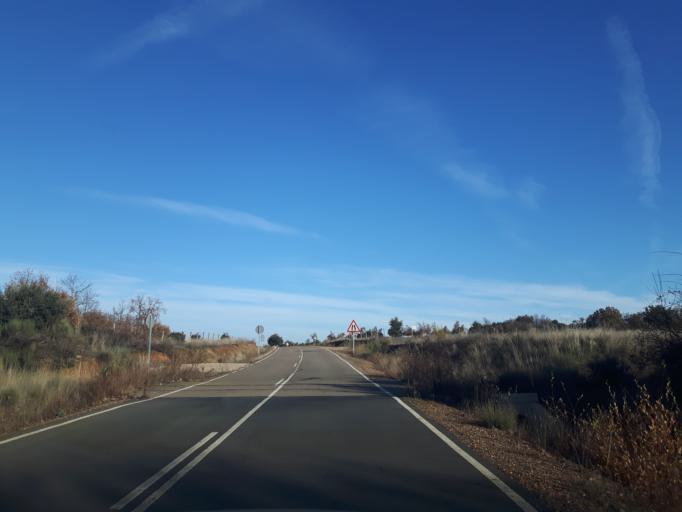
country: ES
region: Castille and Leon
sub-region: Provincia de Salamanca
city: Olmedo de Camaces
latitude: 40.9064
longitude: -6.6182
